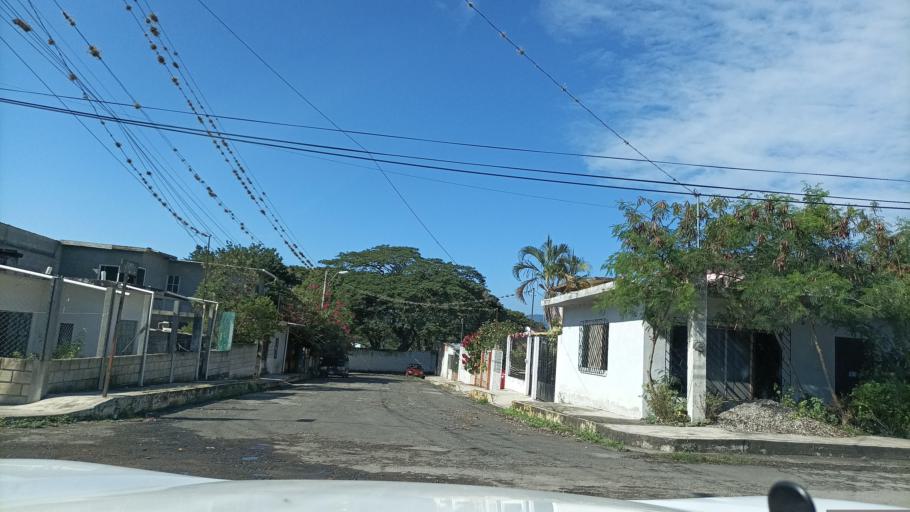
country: MX
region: Veracruz
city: Paso del Macho
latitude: 18.9661
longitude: -96.7189
